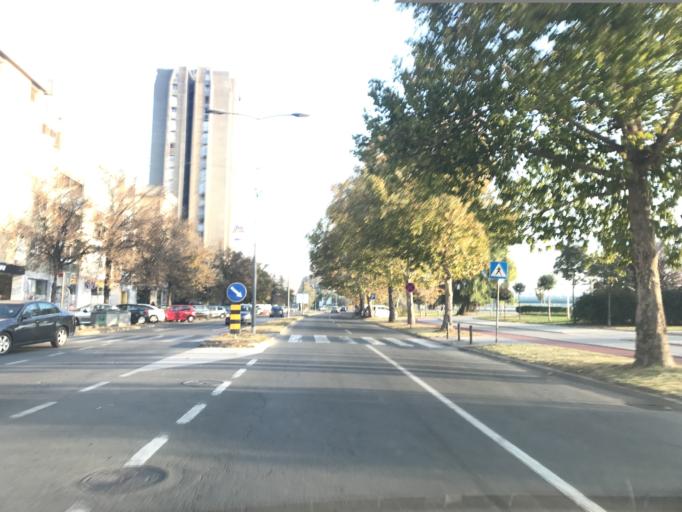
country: RS
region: Autonomna Pokrajina Vojvodina
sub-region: Juznobacki Okrug
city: Novi Sad
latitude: 45.2592
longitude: 19.8552
